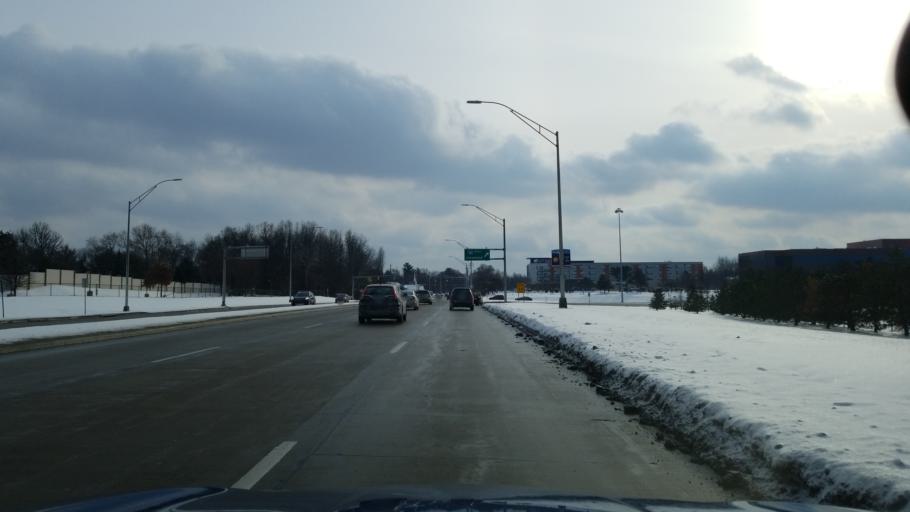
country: US
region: Ohio
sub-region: Cuyahoga County
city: North Olmsted
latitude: 41.4124
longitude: -81.9022
